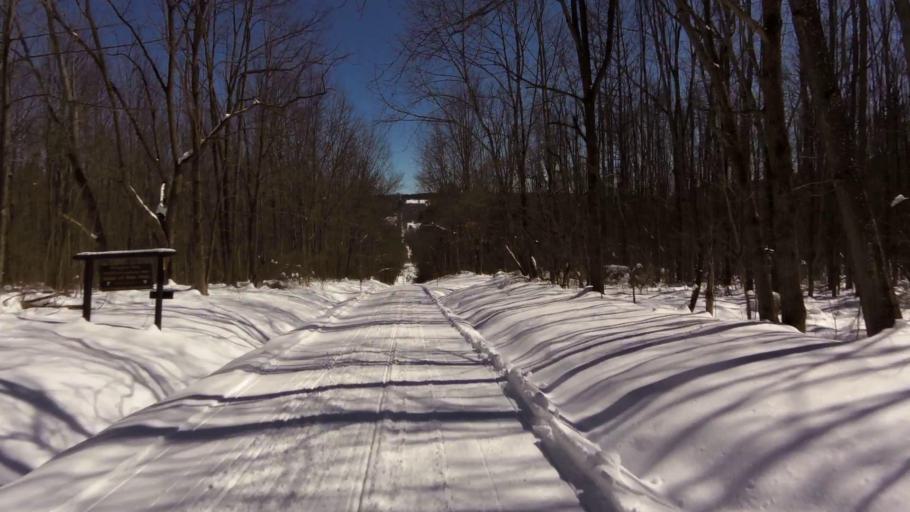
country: US
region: New York
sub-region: Allegany County
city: Houghton
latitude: 42.3267
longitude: -78.2076
